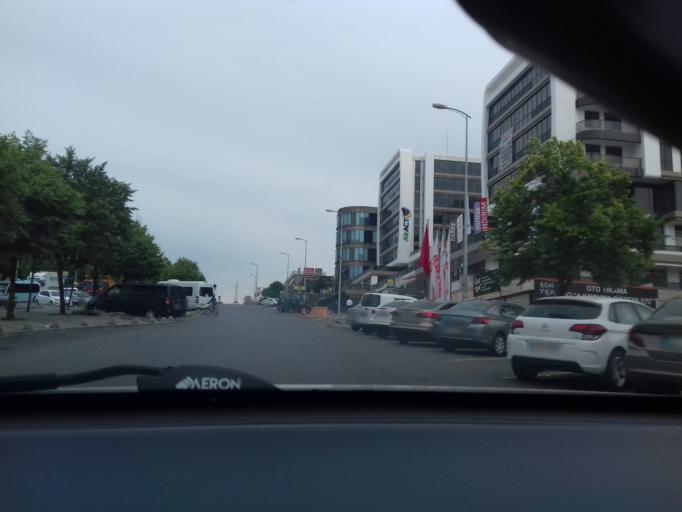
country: TR
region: Istanbul
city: Sultanbeyli
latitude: 40.9280
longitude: 29.3071
